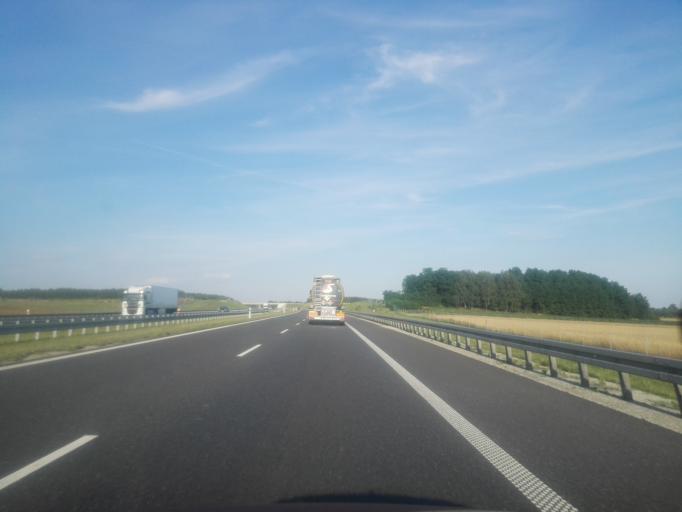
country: PL
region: Lodz Voivodeship
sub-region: Powiat wieruszowski
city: Wieruszow
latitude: 51.3052
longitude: 18.2015
